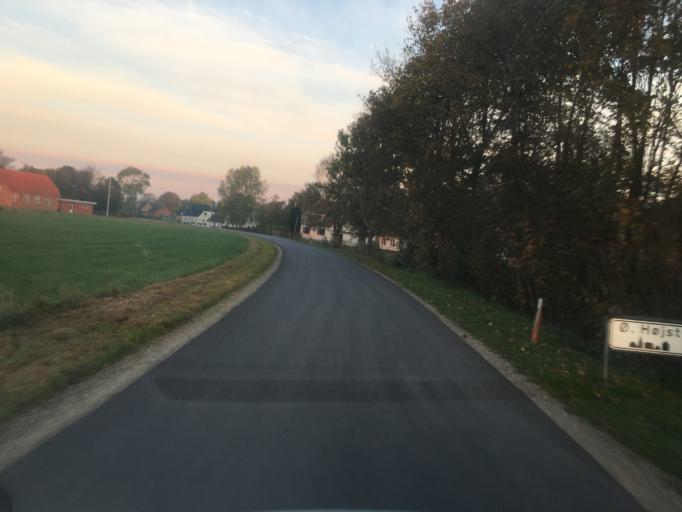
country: DK
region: South Denmark
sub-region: Tonder Kommune
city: Logumkloster
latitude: 54.9987
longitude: 9.0446
